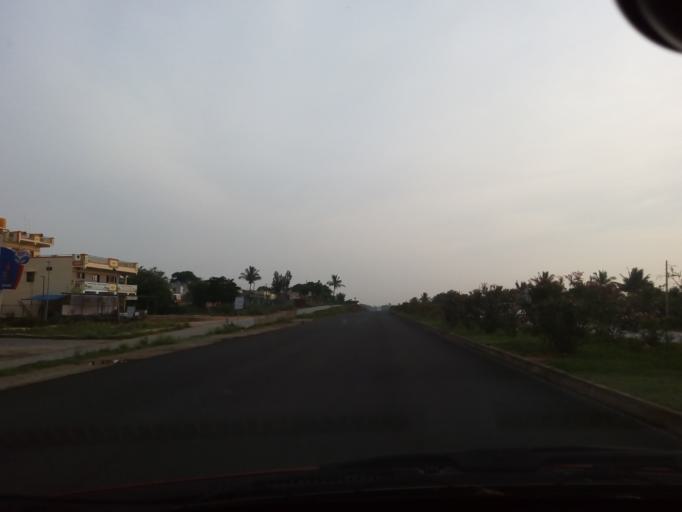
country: IN
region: Karnataka
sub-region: Chikkaballapur
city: Gudibanda
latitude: 13.5918
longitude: 77.7843
